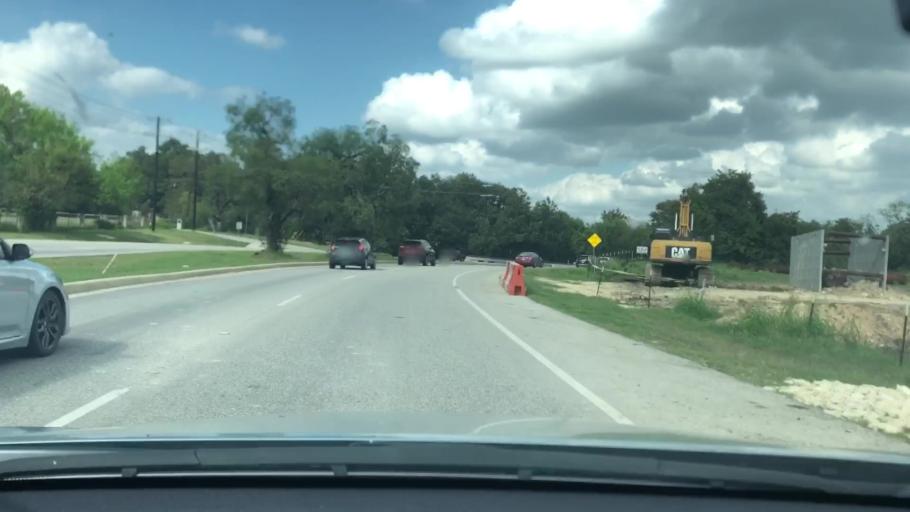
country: US
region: Texas
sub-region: Kendall County
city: Boerne
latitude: 29.7862
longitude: -98.7176
